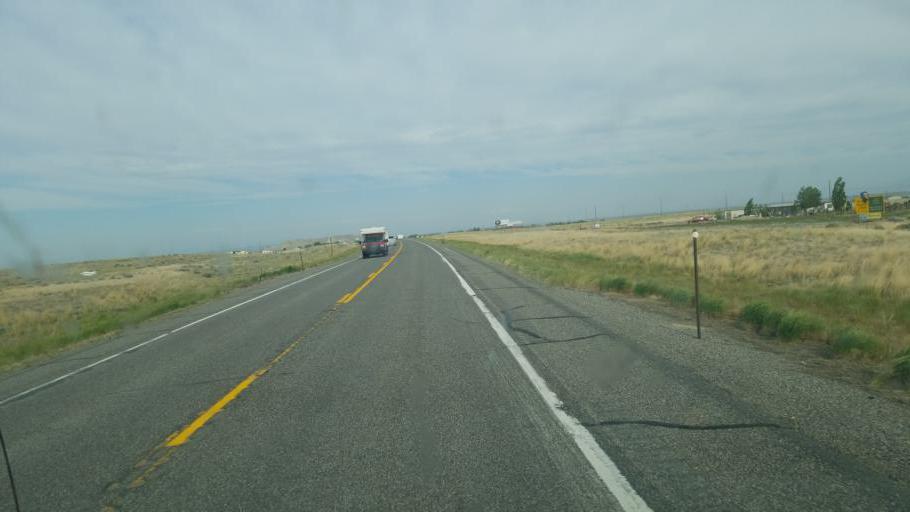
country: US
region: Wyoming
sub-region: Fremont County
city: Riverton
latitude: 43.2369
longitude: -108.0860
